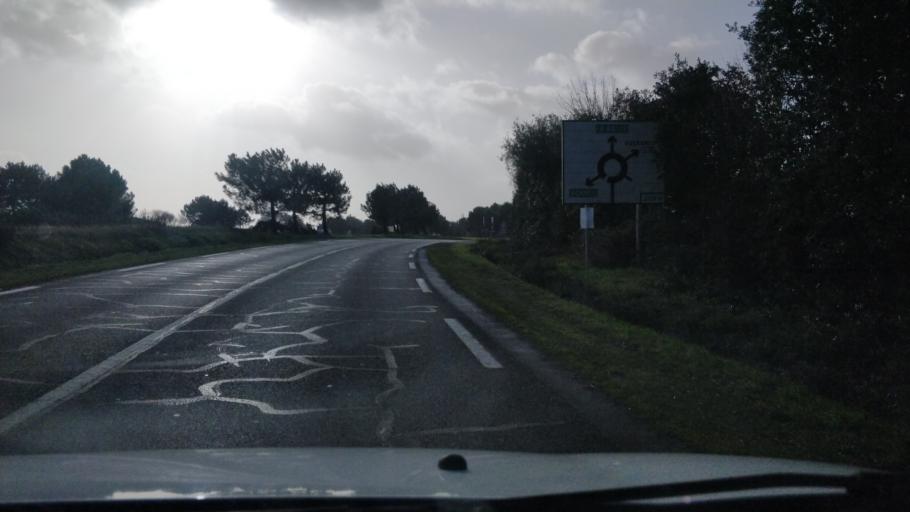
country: FR
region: Pays de la Loire
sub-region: Departement de la Loire-Atlantique
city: Guerande
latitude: 47.3437
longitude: -2.4281
